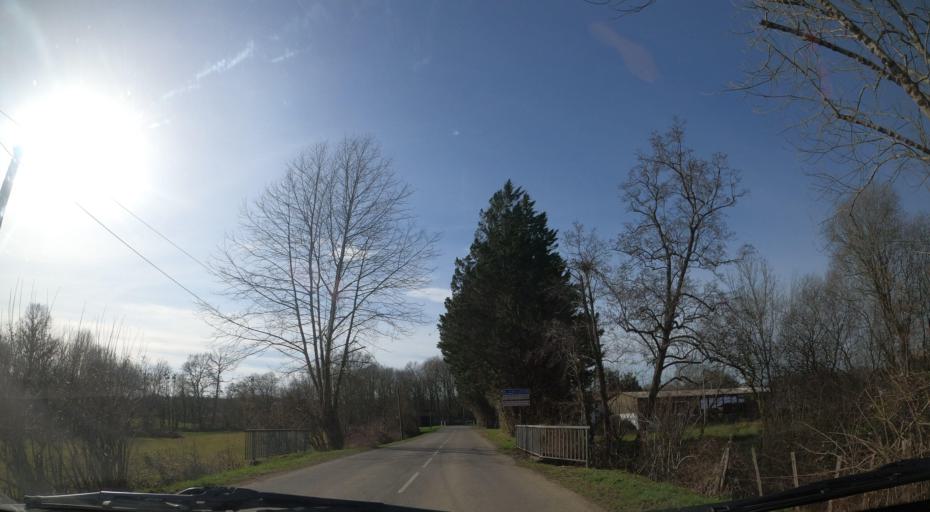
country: FR
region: Aquitaine
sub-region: Departement des Pyrenees-Atlantiques
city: Lahonce
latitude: 43.4518
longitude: -1.3776
